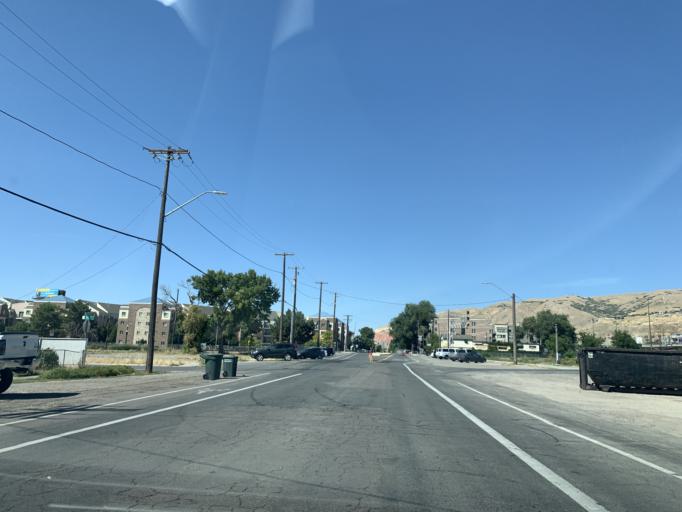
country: US
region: Utah
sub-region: Salt Lake County
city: Salt Lake City
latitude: 40.7680
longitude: -111.9082
